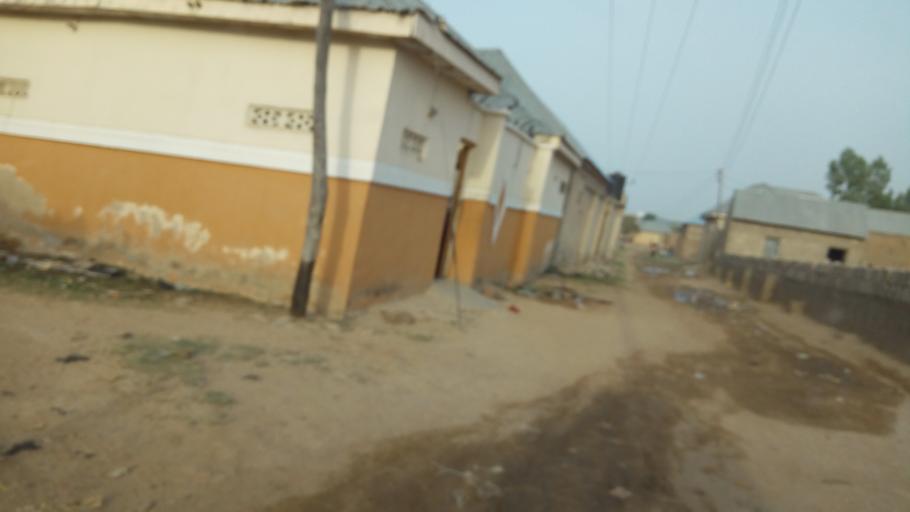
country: NG
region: Gombe
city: Gombe
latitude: 10.2574
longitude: 11.1851
